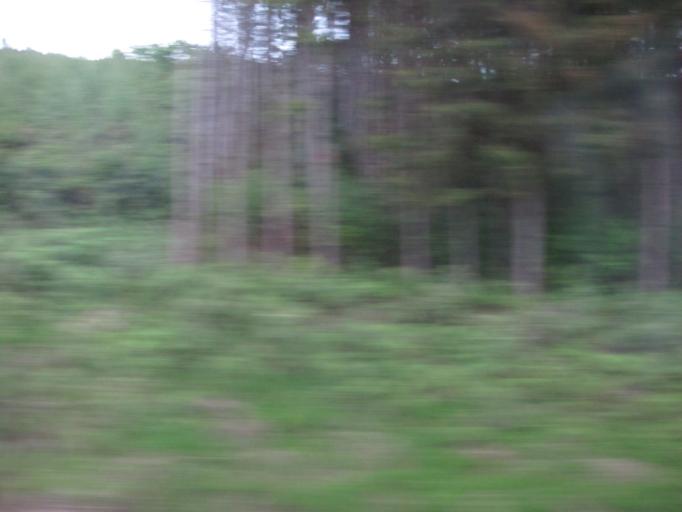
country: NO
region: Oppland
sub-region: Lillehammer
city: Lillehammer
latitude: 61.1575
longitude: 10.4048
